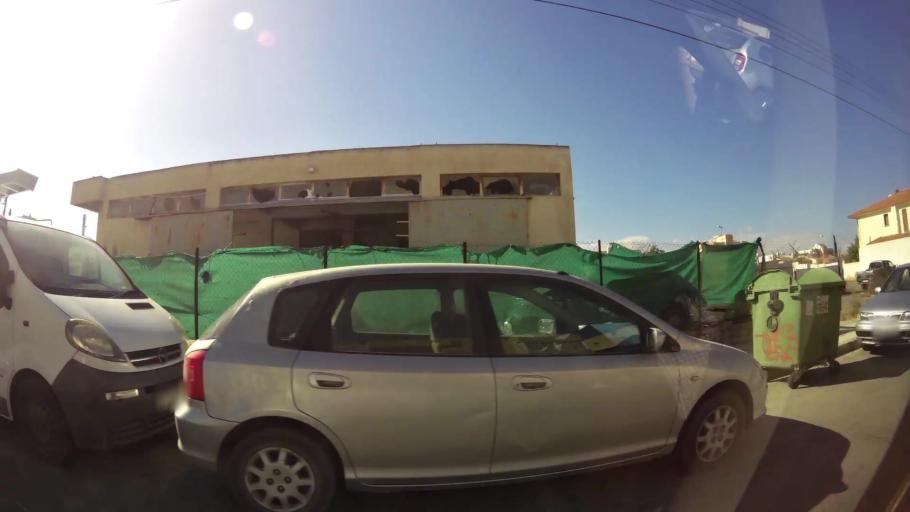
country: CY
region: Lefkosia
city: Nicosia
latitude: 35.1321
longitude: 33.3387
